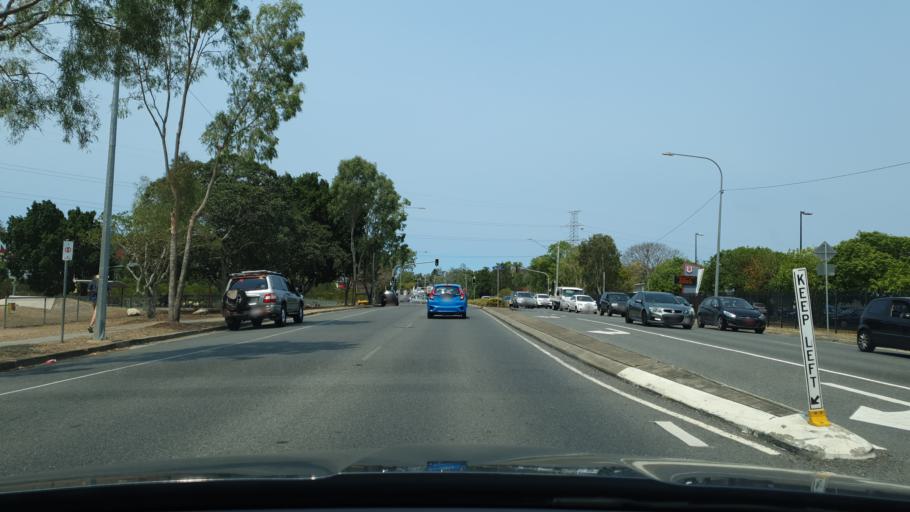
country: AU
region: Queensland
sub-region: Ipswich
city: Bundamba
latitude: -27.6113
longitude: 152.8037
